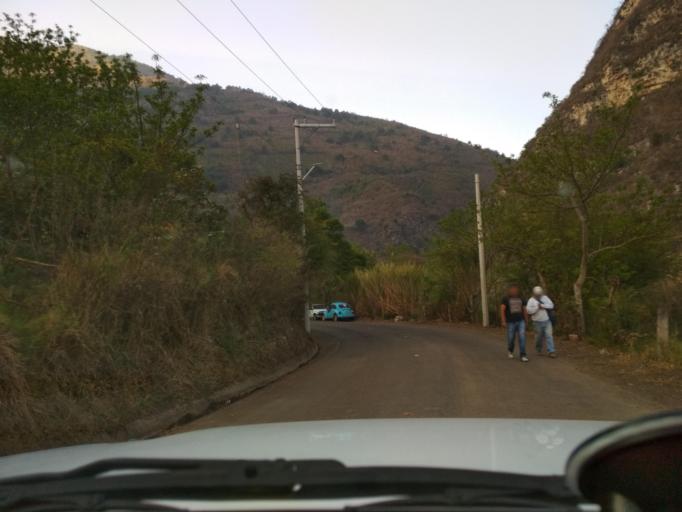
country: MX
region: Veracruz
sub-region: Nogales
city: Taza de Agua Ojo Zarco
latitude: 18.7739
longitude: -97.1954
